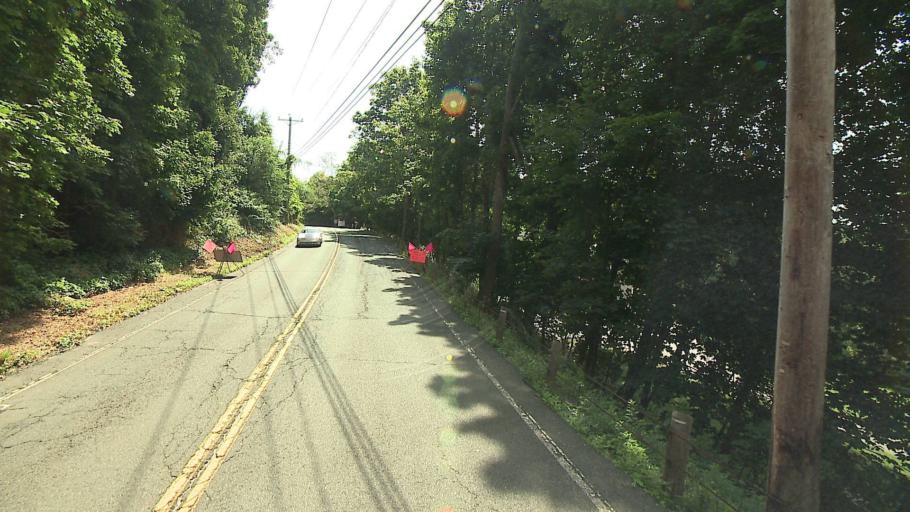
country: US
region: New York
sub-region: Putnam County
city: Putnam Lake
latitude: 41.4685
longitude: -73.5185
